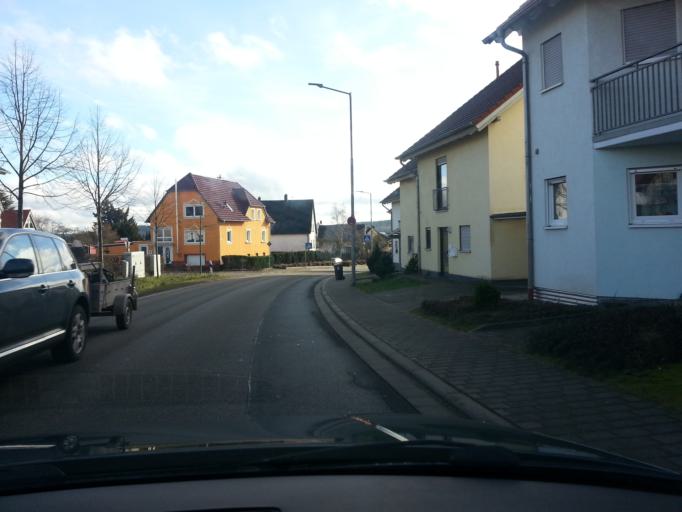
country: DE
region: Rheinland-Pfalz
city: Rodenbach
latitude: 49.4706
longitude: 7.6822
